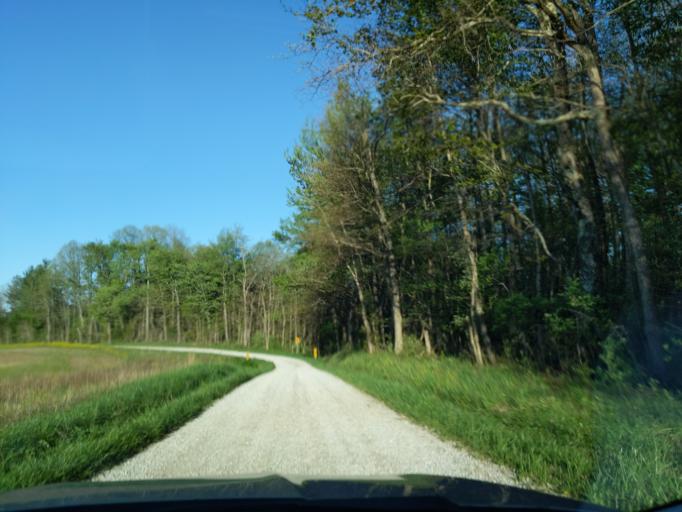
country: US
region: Indiana
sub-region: Decatur County
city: Westport
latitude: 39.2002
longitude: -85.4382
